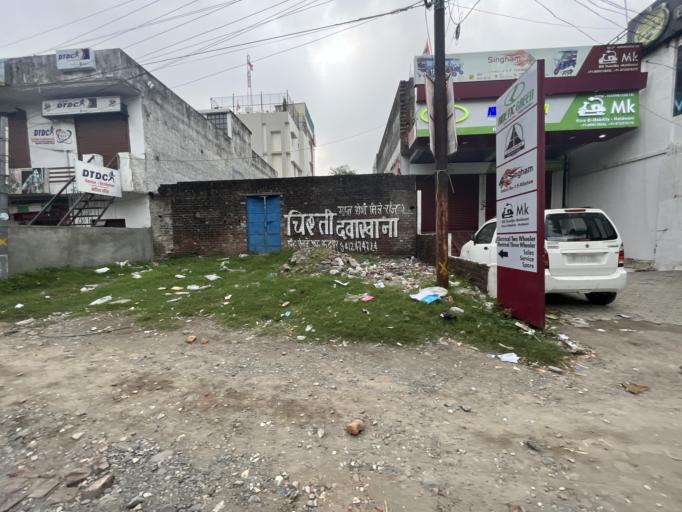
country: IN
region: Uttarakhand
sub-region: Naini Tal
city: Haldwani
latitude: 29.2003
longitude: 79.5148
